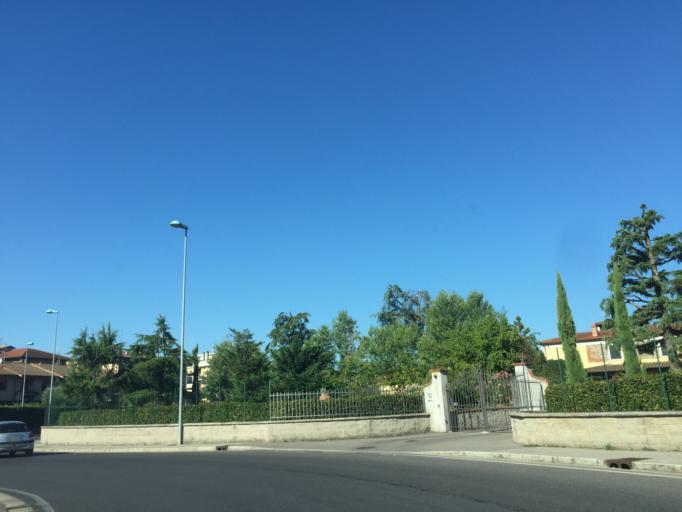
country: IT
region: Tuscany
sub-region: Provincia di Pistoia
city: Pistoia
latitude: 43.9440
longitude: 10.9196
